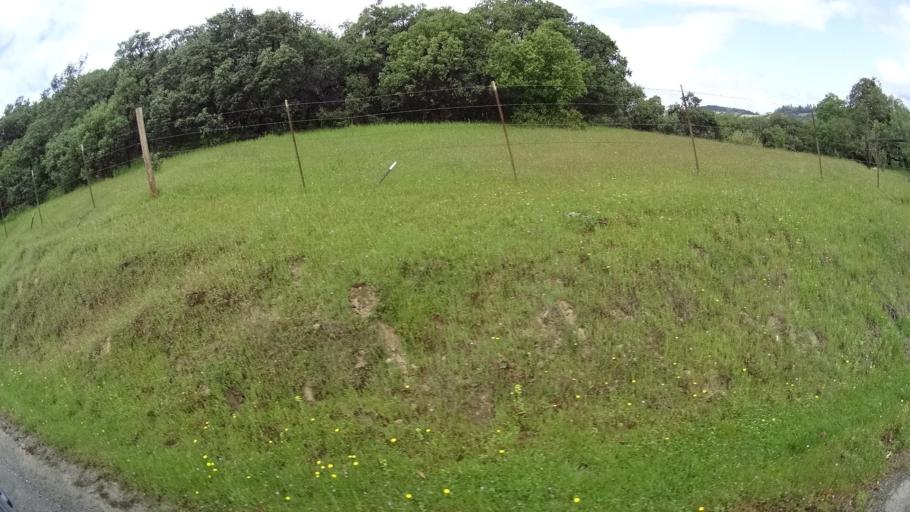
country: US
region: California
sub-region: Humboldt County
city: Redway
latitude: 40.1665
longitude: -123.6109
